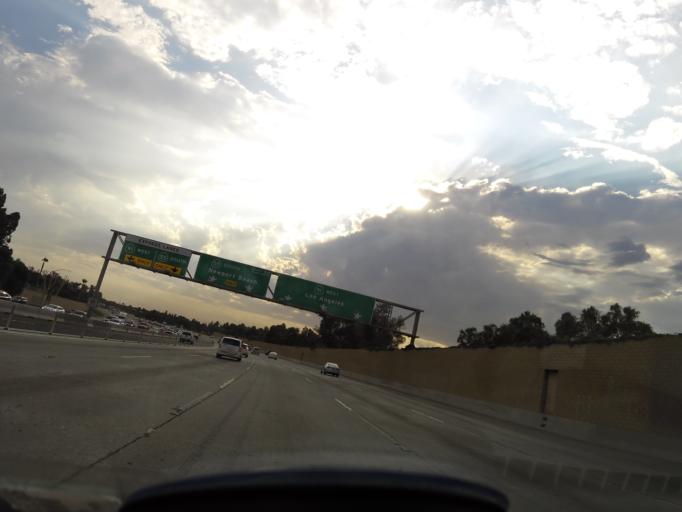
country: US
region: California
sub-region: Orange County
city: Yorba Linda
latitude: 33.8545
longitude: -117.8082
